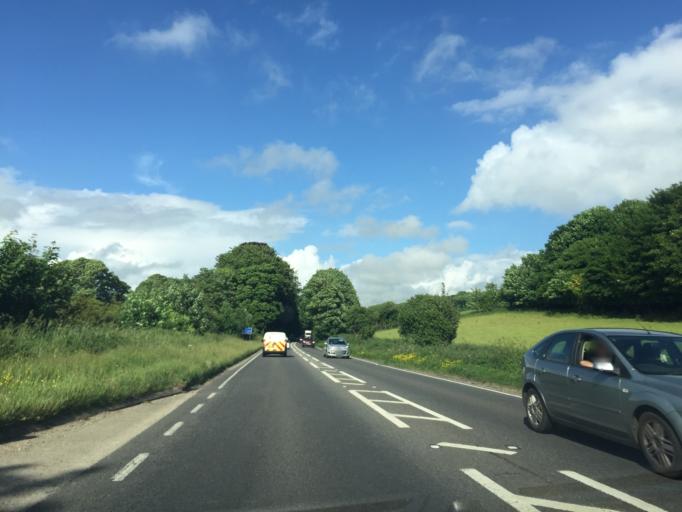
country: GB
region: England
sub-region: Dorset
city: Dorchester
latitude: 50.7329
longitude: -2.3993
